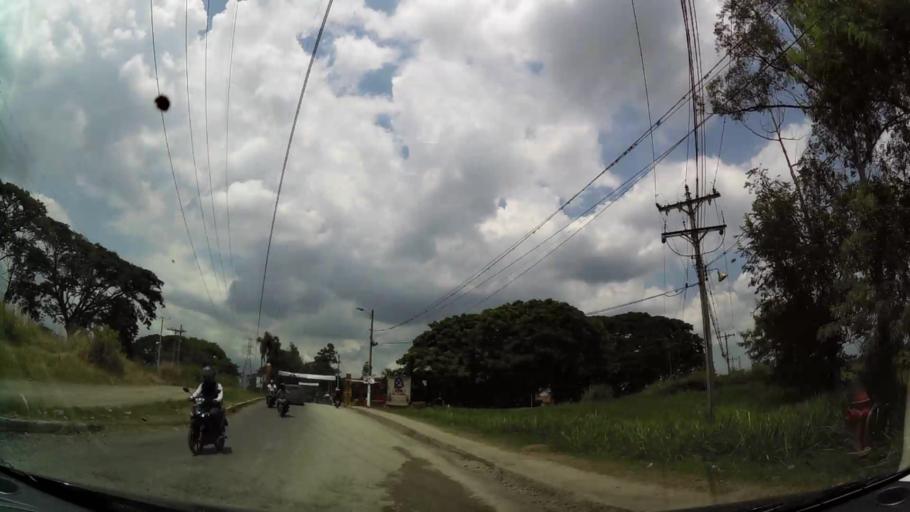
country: CO
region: Valle del Cauca
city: Cali
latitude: 3.4545
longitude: -76.4711
